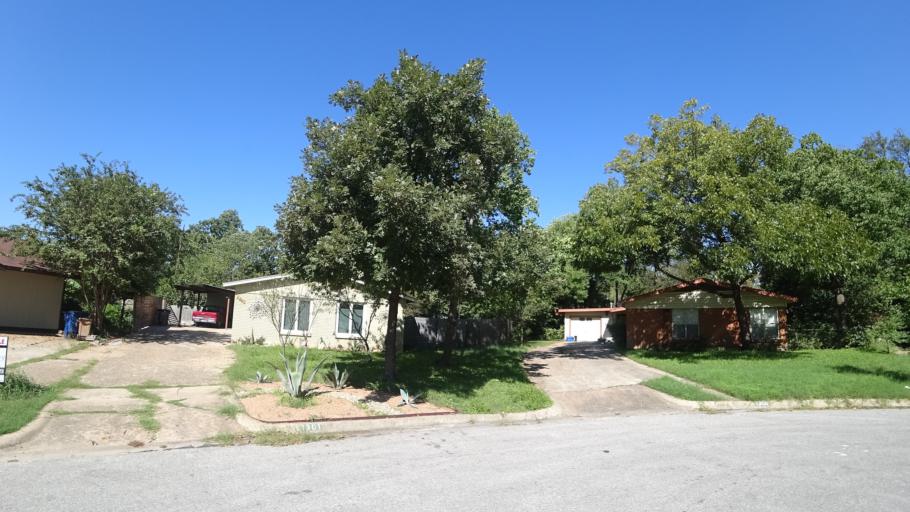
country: US
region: Texas
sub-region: Travis County
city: Austin
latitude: 30.3105
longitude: -97.7024
